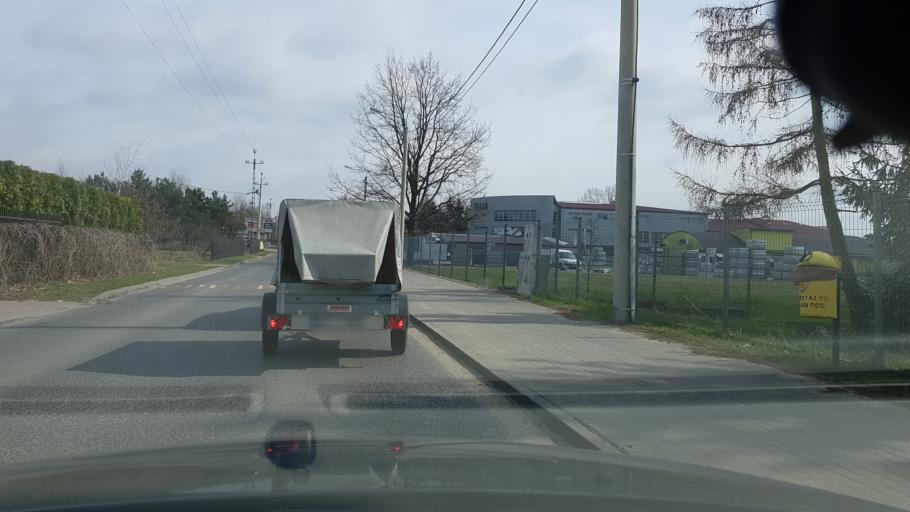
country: PL
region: Masovian Voivodeship
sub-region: Warszawa
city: Wesola
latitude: 52.2249
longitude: 21.2340
